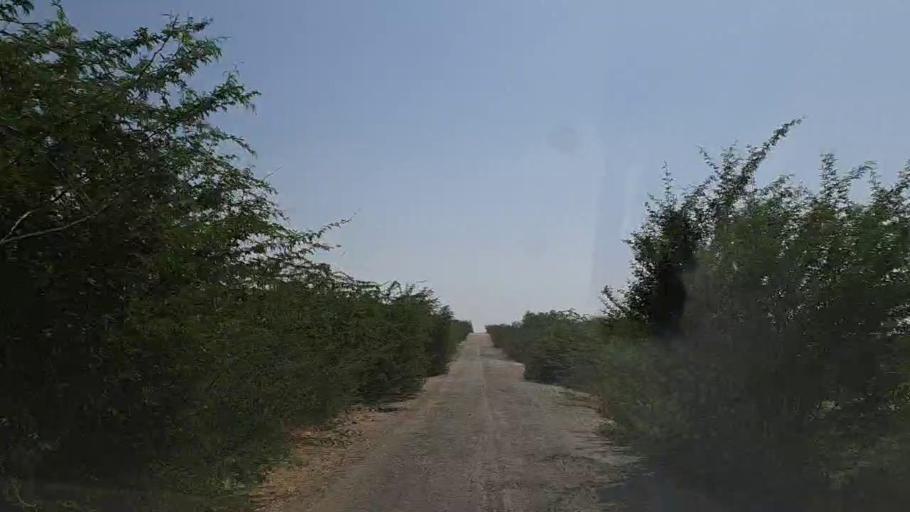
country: PK
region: Sindh
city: Diplo
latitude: 24.4977
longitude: 69.4307
